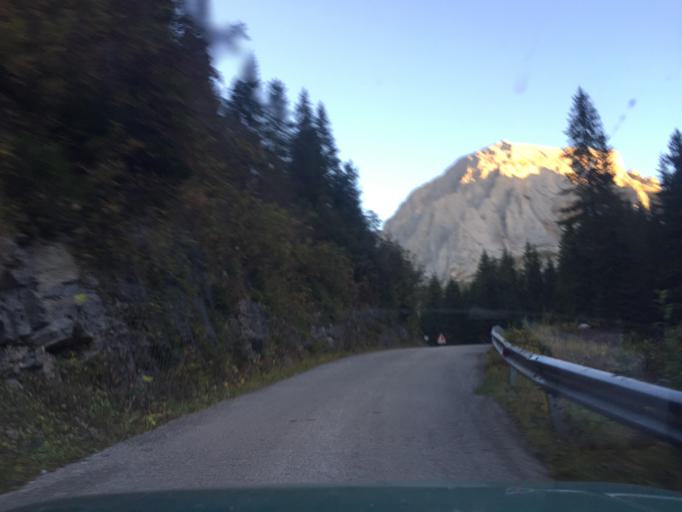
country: IT
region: Veneto
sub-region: Provincia di Belluno
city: Granvilla
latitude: 46.6070
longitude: 12.7212
